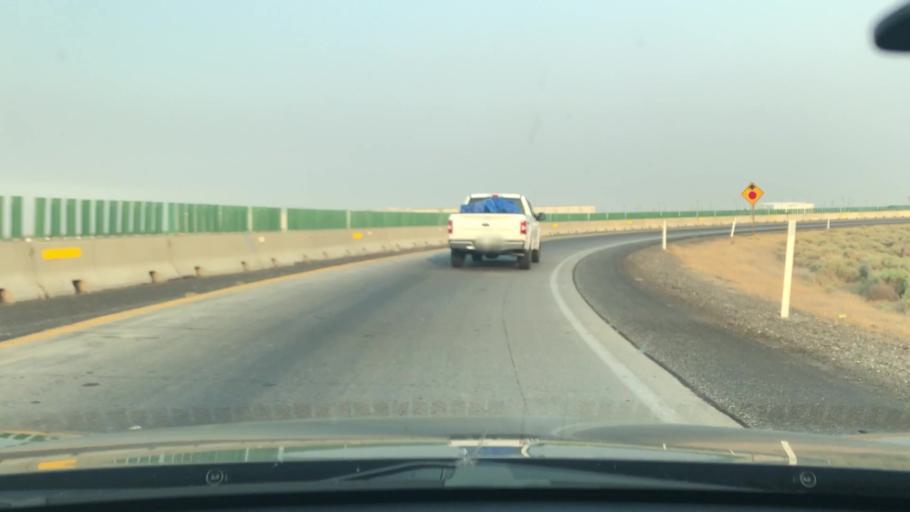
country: US
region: Washington
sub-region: Franklin County
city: Pasco
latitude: 46.2668
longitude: -119.0847
